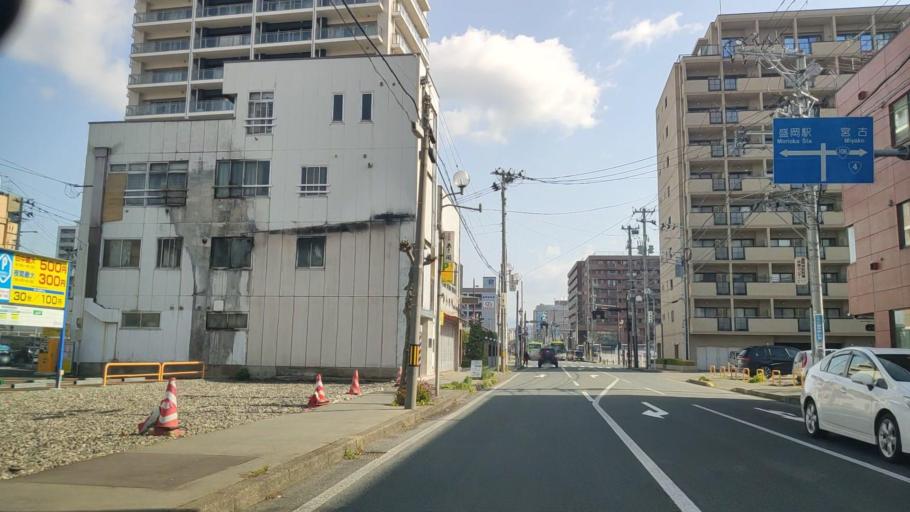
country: JP
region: Iwate
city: Morioka-shi
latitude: 39.6986
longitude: 141.1569
